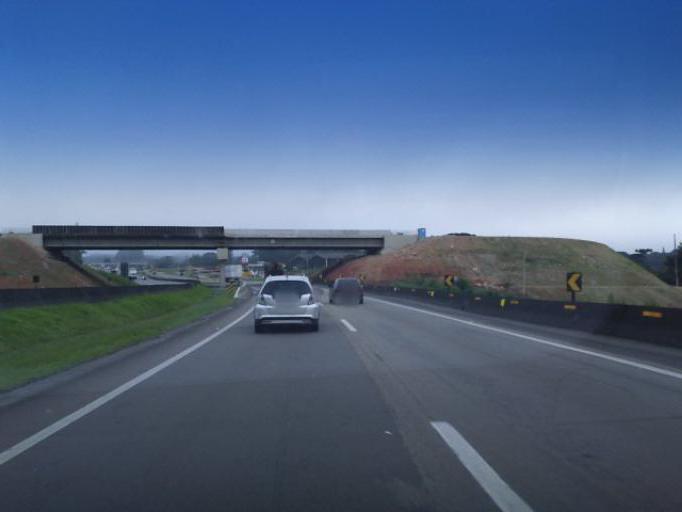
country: BR
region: Parana
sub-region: Sao Jose Dos Pinhais
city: Sao Jose dos Pinhais
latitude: -25.8210
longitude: -49.1281
